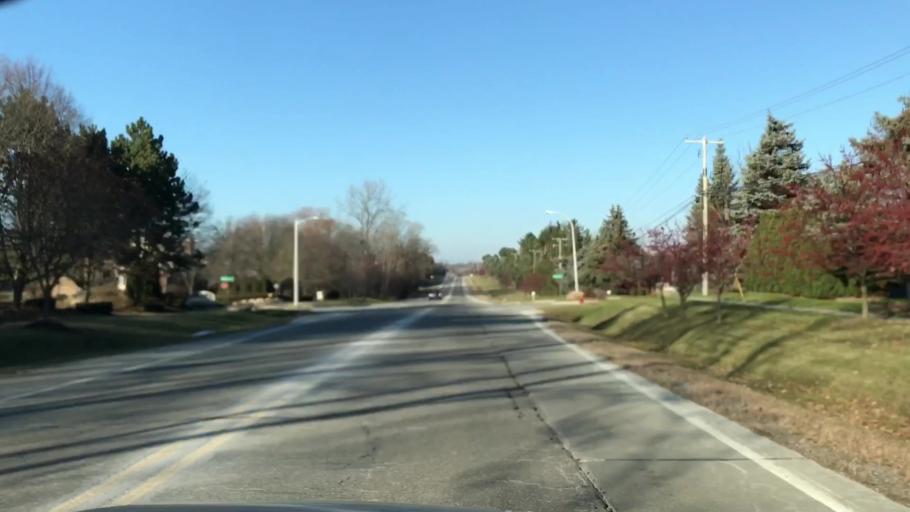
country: US
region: Michigan
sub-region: Wayne County
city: Northville
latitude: 42.4529
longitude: -83.4941
